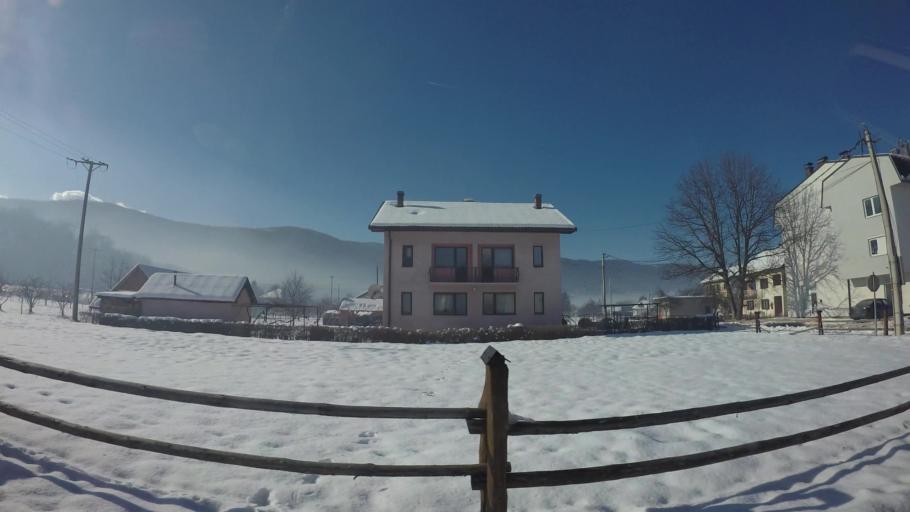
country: BA
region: Federation of Bosnia and Herzegovina
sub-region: Kanton Sarajevo
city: Sarajevo
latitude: 43.7933
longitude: 18.3533
